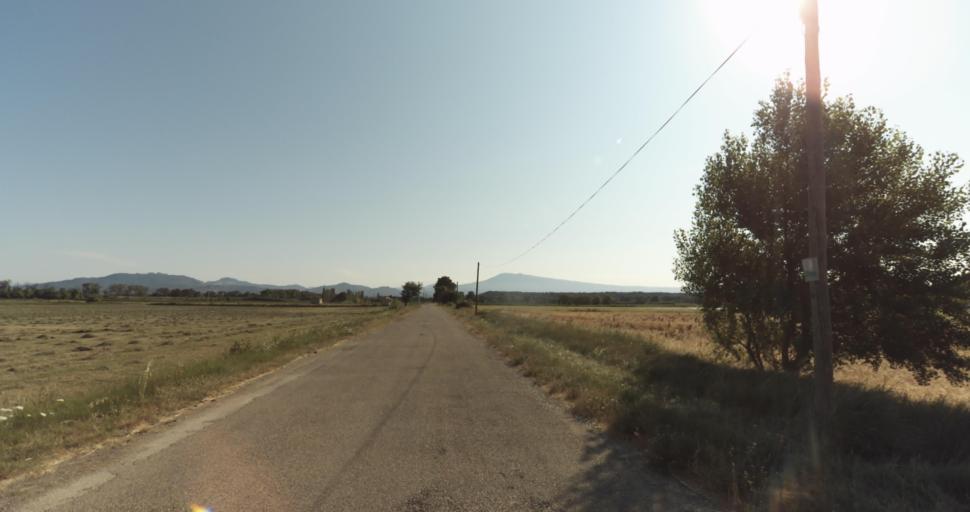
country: FR
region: Provence-Alpes-Cote d'Azur
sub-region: Departement du Vaucluse
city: Sarrians
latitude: 44.0564
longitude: 4.9690
